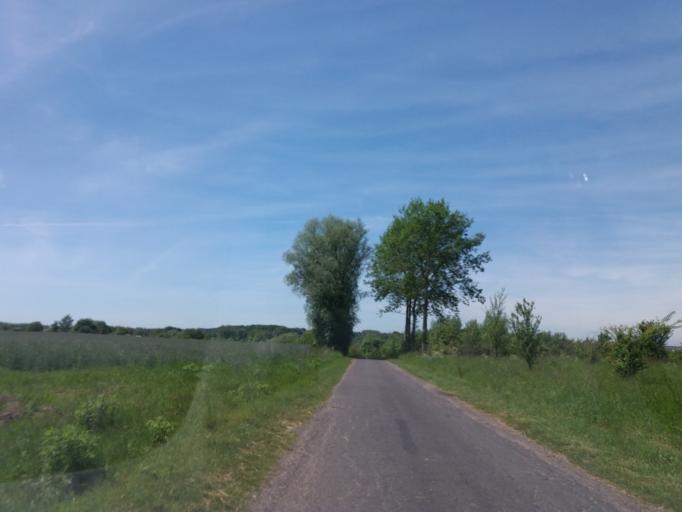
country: PL
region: West Pomeranian Voivodeship
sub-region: Powiat stargardzki
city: Dobrzany
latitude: 53.3529
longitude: 15.4358
